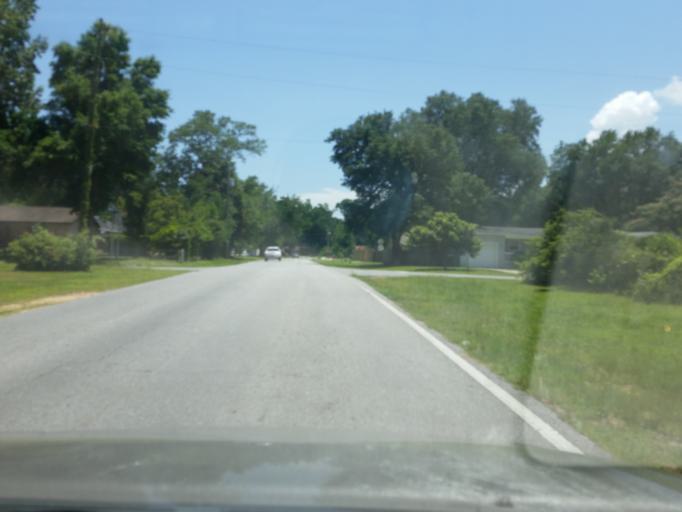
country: US
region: Florida
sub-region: Escambia County
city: Ferry Pass
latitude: 30.5157
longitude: -87.1940
